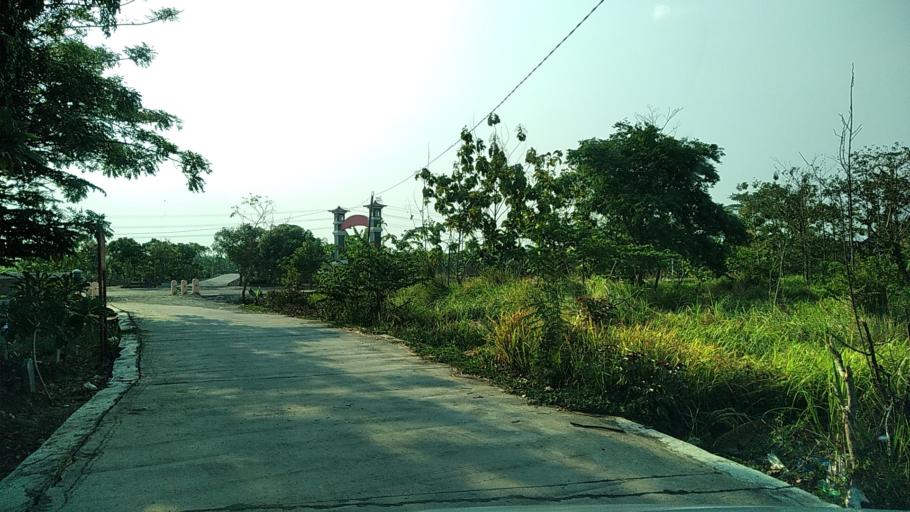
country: ID
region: Central Java
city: Mranggen
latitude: -6.9662
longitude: 110.4901
